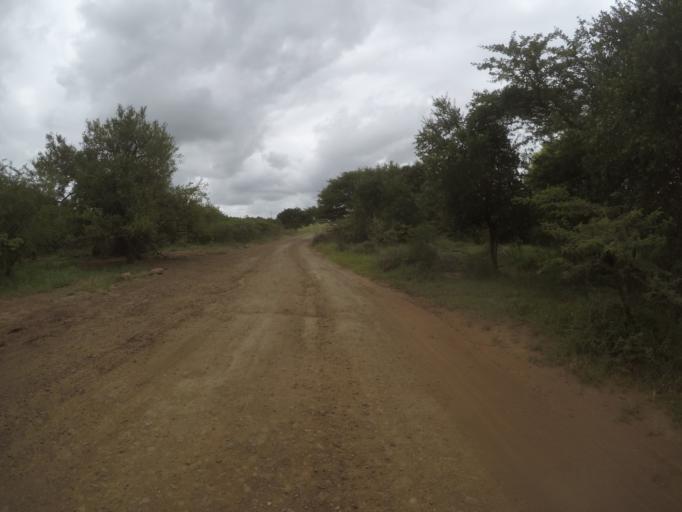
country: ZA
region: KwaZulu-Natal
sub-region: uThungulu District Municipality
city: Empangeni
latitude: -28.5632
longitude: 31.8727
